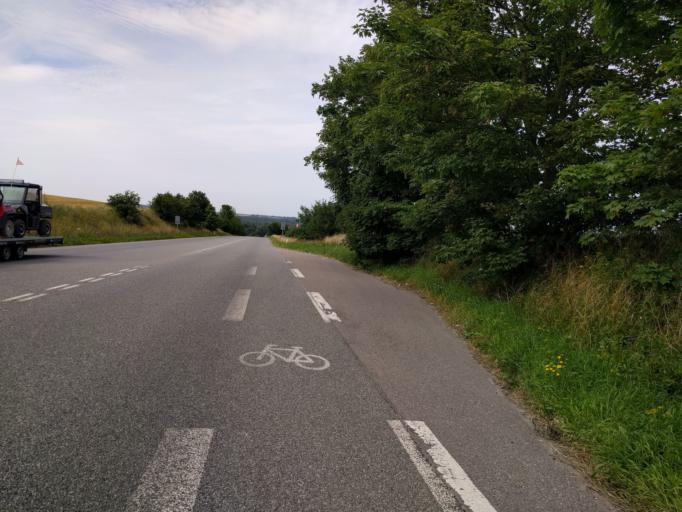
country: DK
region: Zealand
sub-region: Kalundborg Kommune
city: Svebolle
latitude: 55.6919
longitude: 11.3241
